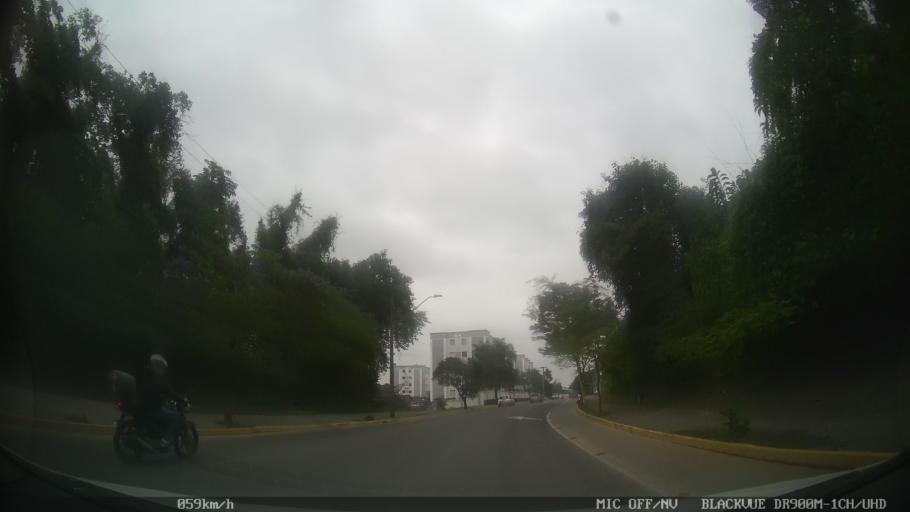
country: BR
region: Santa Catarina
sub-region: Joinville
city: Joinville
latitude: -26.3422
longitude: -48.8428
